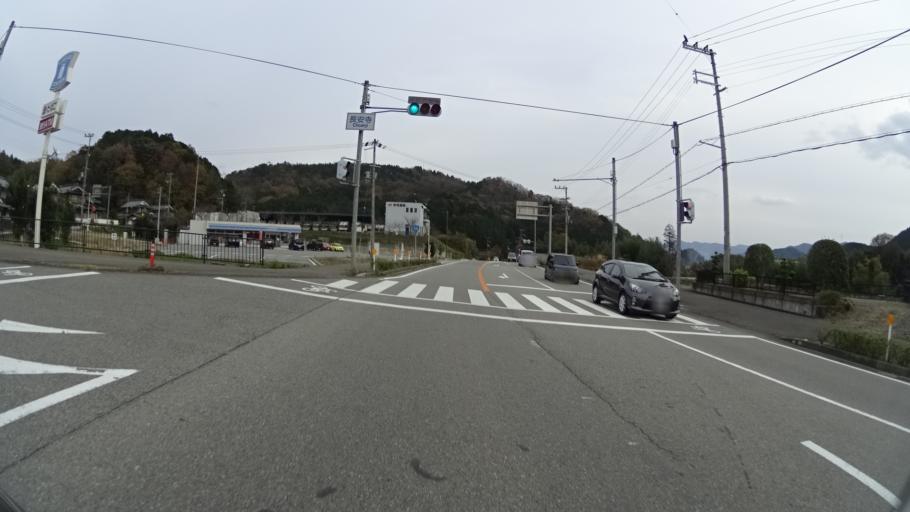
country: JP
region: Hyogo
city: Sasayama
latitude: 35.0931
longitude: 135.1532
